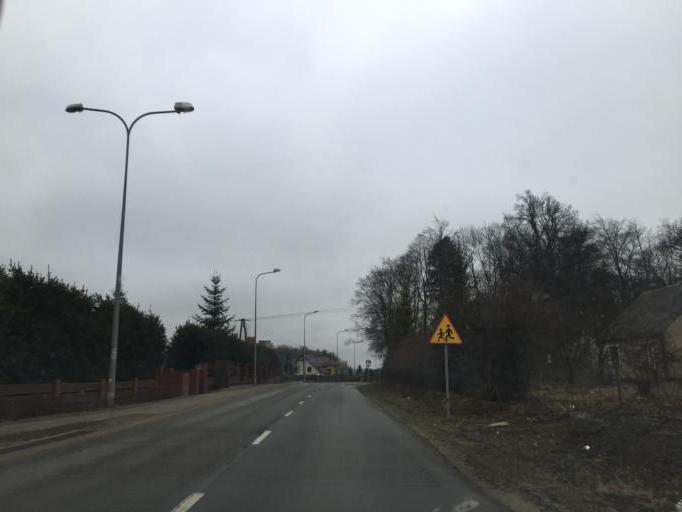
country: PL
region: Pomeranian Voivodeship
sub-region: Powiat kartuski
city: Banino
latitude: 54.3696
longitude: 18.3998
